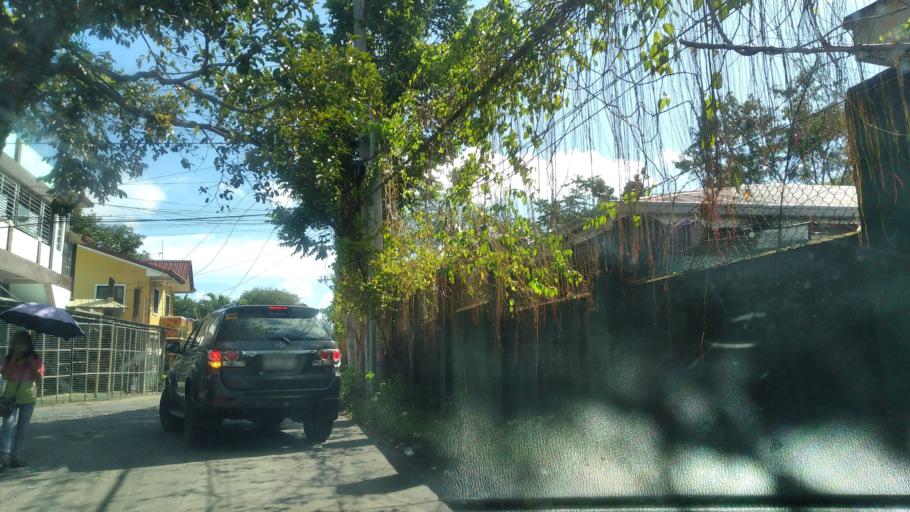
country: PH
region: Calabarzon
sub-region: Province of Quezon
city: Lucena
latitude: 13.9430
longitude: 121.6121
